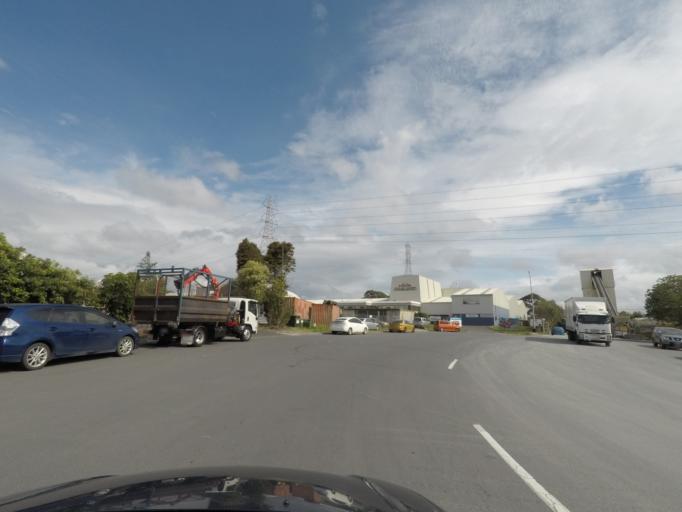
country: NZ
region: Auckland
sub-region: Auckland
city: Rosebank
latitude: -36.8505
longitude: 174.6398
